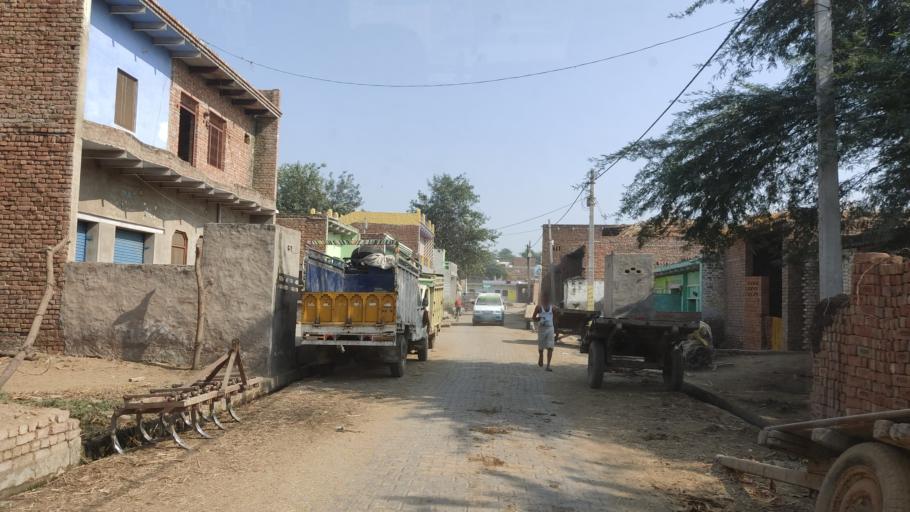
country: IN
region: Uttar Pradesh
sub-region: Mathura
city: Radha Kund
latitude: 27.5569
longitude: 77.5585
